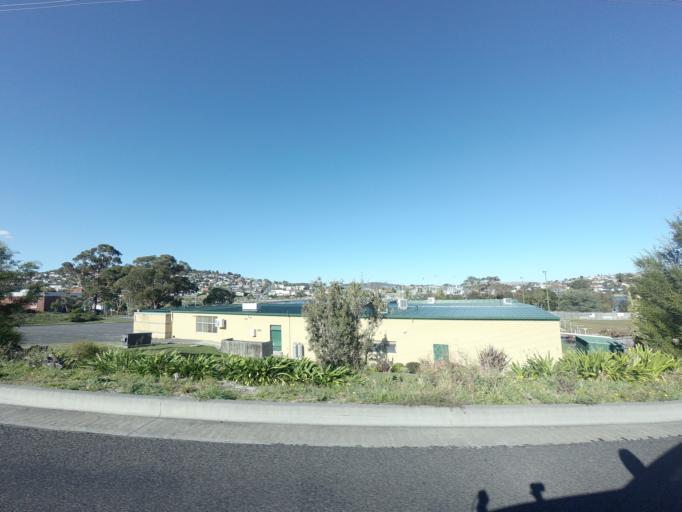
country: AU
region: Tasmania
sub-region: Clarence
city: Bellerive
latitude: -42.8703
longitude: 147.3630
